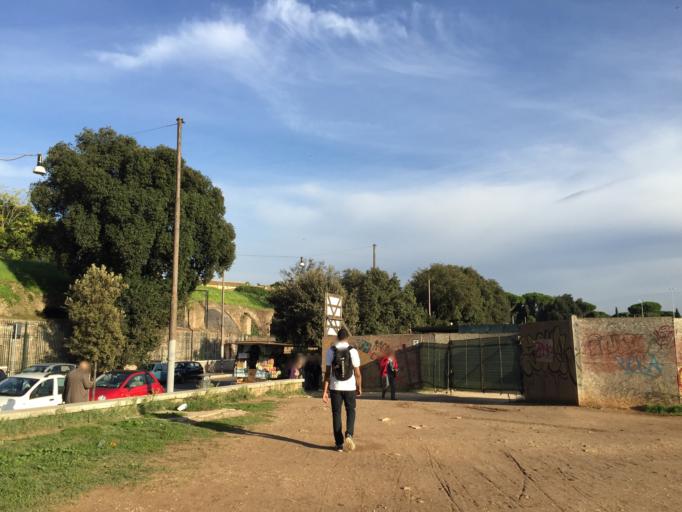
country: IT
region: Latium
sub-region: Citta metropolitana di Roma Capitale
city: Rome
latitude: 41.8858
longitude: 12.4872
